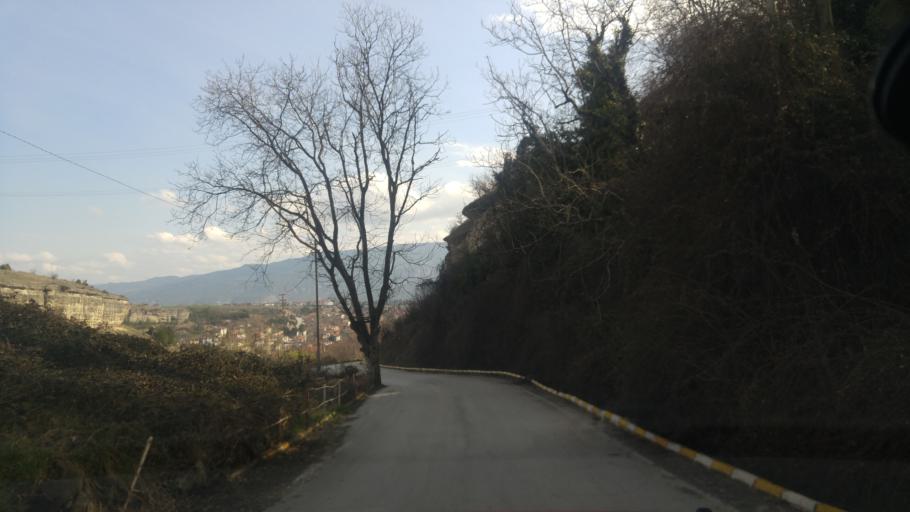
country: TR
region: Karabuk
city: Safranbolu
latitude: 41.2569
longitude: 32.6826
